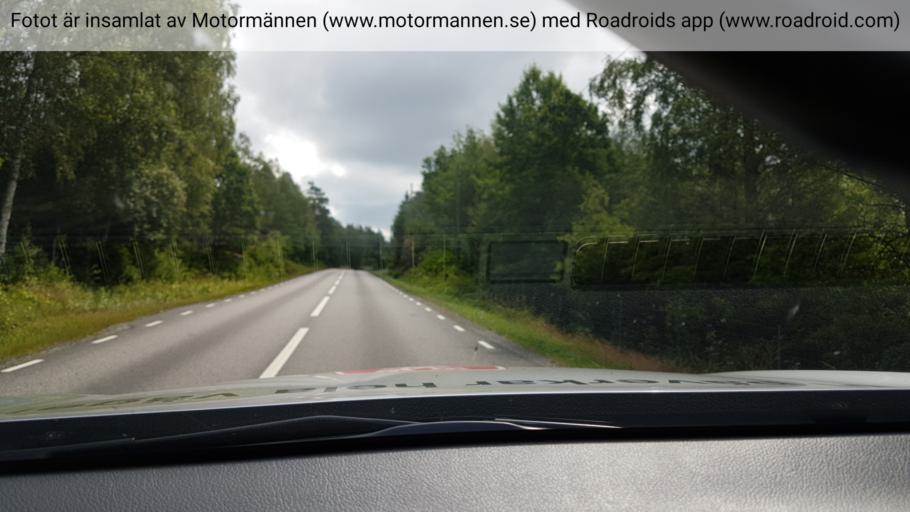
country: SE
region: Vaestra Goetaland
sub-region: Marks Kommun
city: Kinna
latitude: 57.4728
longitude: 12.7229
